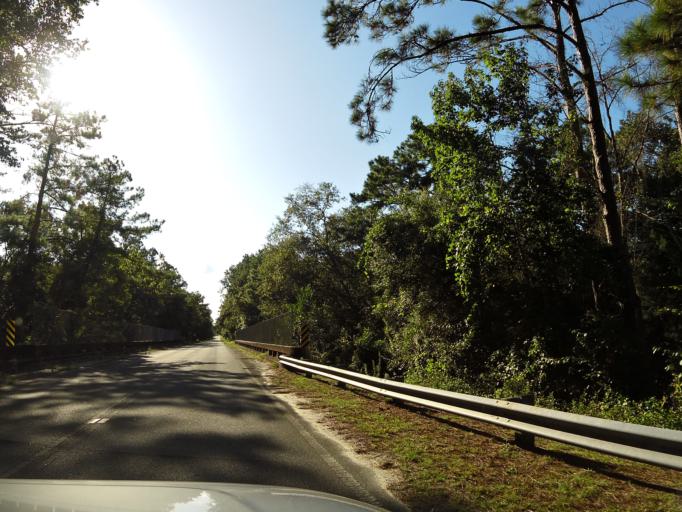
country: US
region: Florida
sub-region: Wakulla County
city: Crawfordville
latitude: 30.0628
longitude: -84.5002
